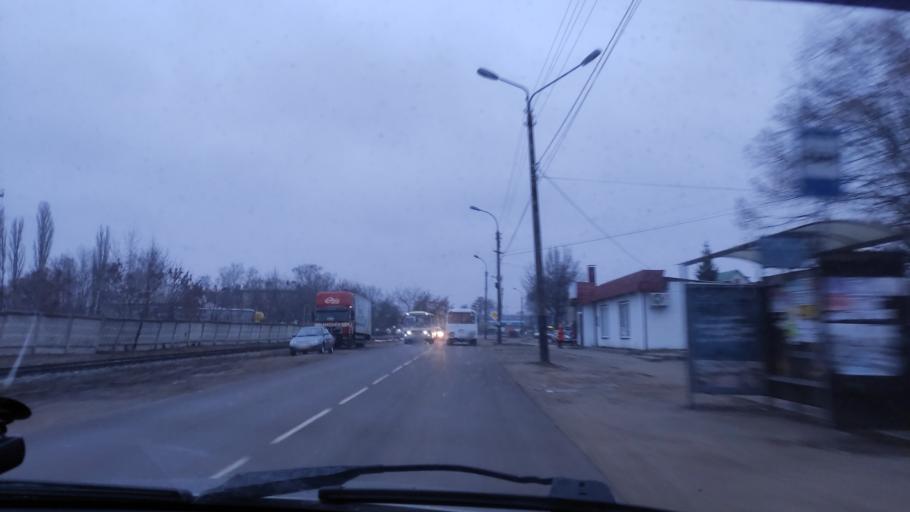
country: RU
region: Tambov
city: Pokrovo-Prigorodnoye
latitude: 52.7189
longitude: 41.3879
